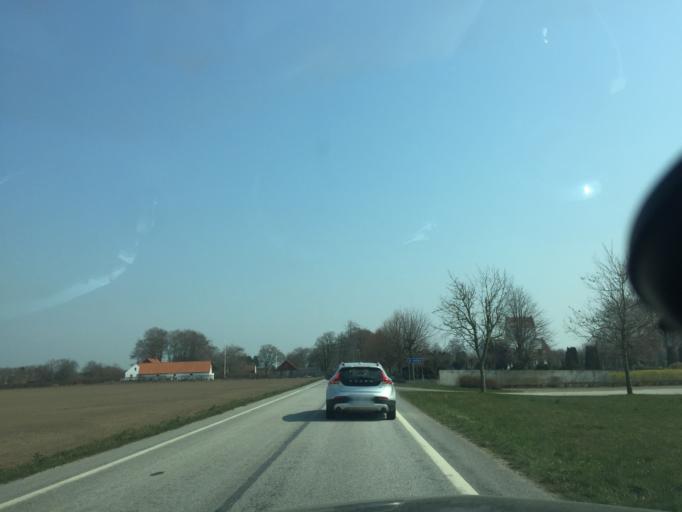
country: SE
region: Skane
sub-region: Simrishamns Kommun
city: Simrishamn
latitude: 55.4721
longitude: 14.2280
